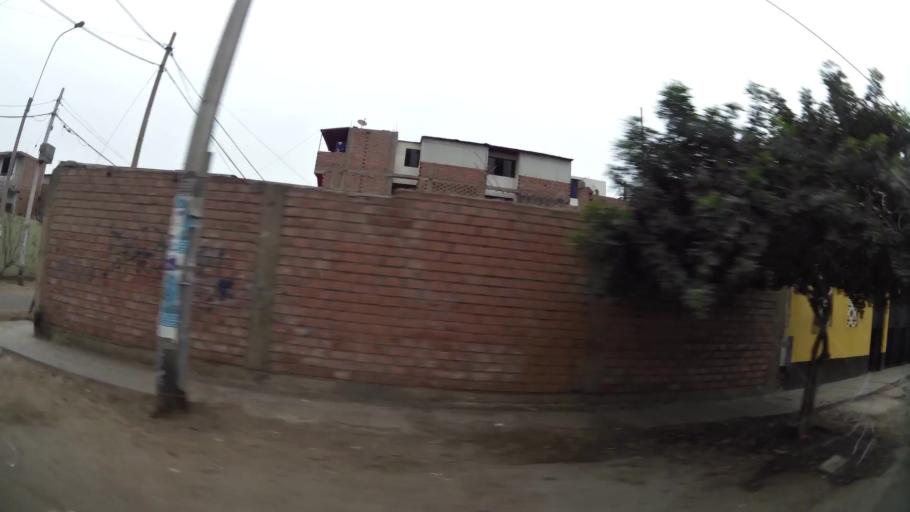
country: PE
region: Lima
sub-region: Lima
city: Surco
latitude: -12.1700
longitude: -76.9755
